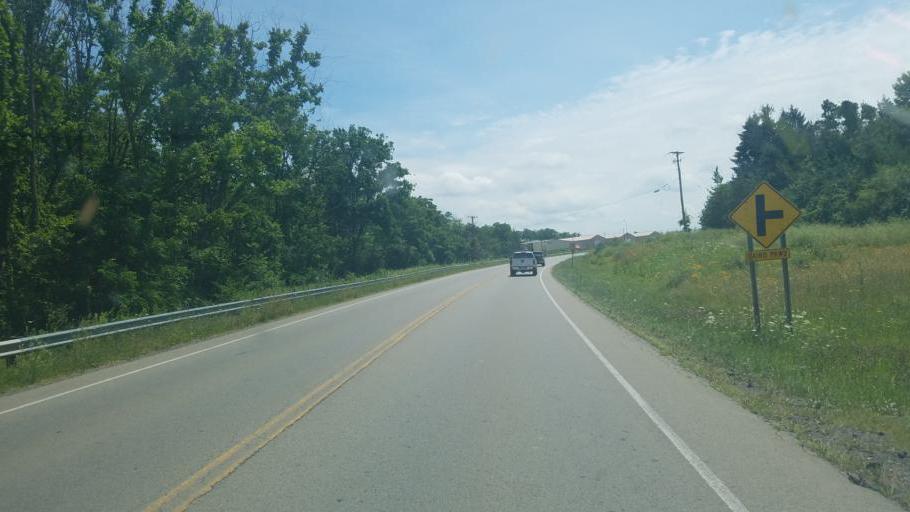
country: US
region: Ohio
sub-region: Richland County
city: Lincoln Heights
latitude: 40.8250
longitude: -82.5021
